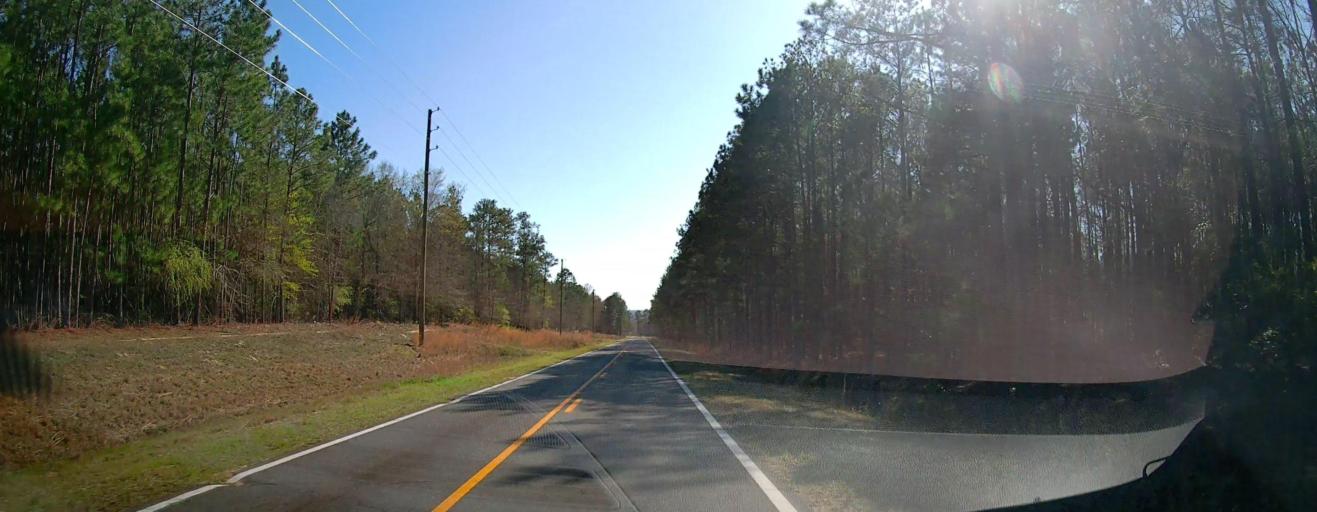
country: US
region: Georgia
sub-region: Taylor County
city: Reynolds
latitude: 32.5783
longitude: -83.9939
